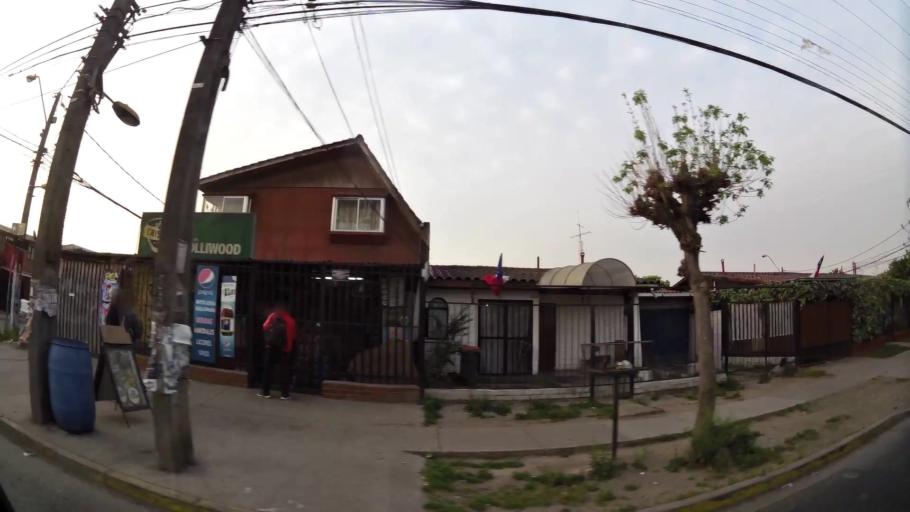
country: CL
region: Santiago Metropolitan
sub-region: Provincia de Santiago
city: Lo Prado
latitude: -33.5183
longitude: -70.7824
